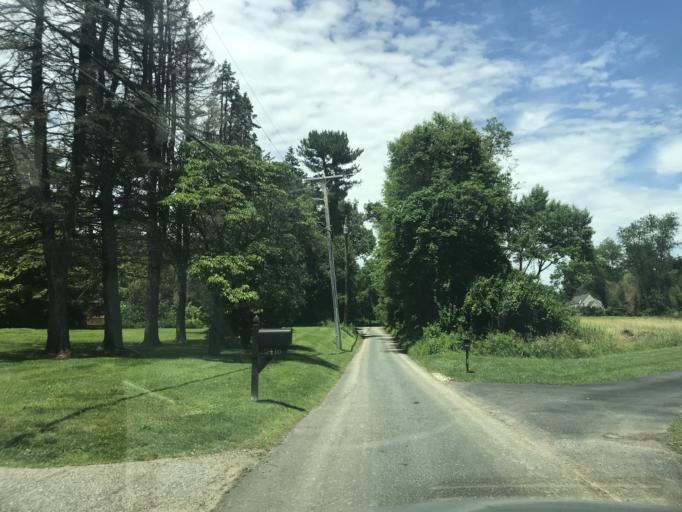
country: US
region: Maryland
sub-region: Baltimore County
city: Kingsville
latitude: 39.4653
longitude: -76.4515
